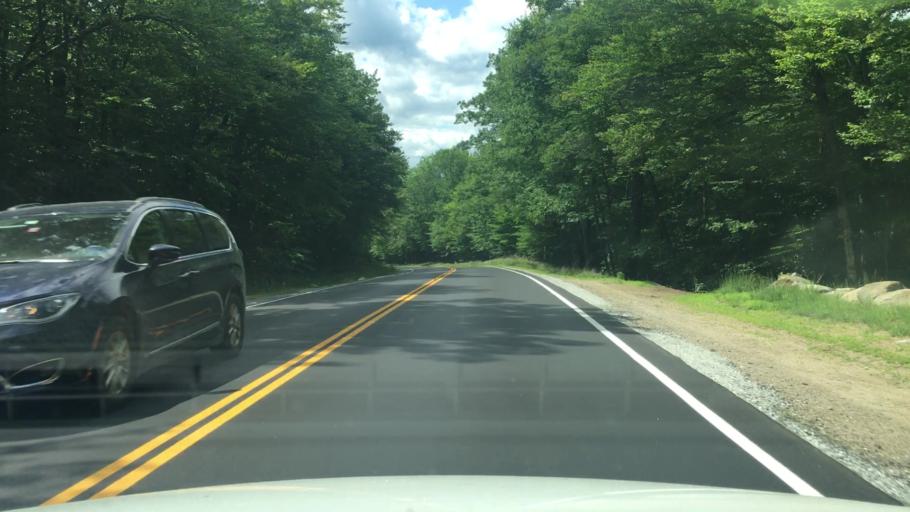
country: US
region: Maine
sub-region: Oxford County
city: Bethel
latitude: 44.3971
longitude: -70.6702
